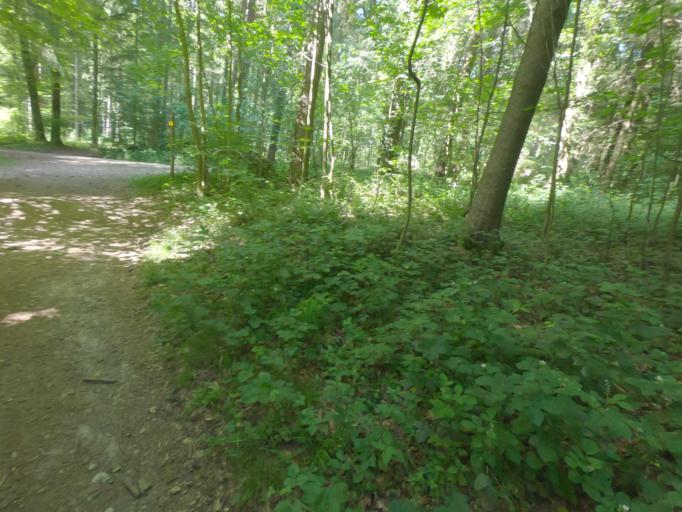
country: CH
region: Solothurn
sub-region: Bezirk Solothurn
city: Solothurn
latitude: 47.2289
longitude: 7.5368
